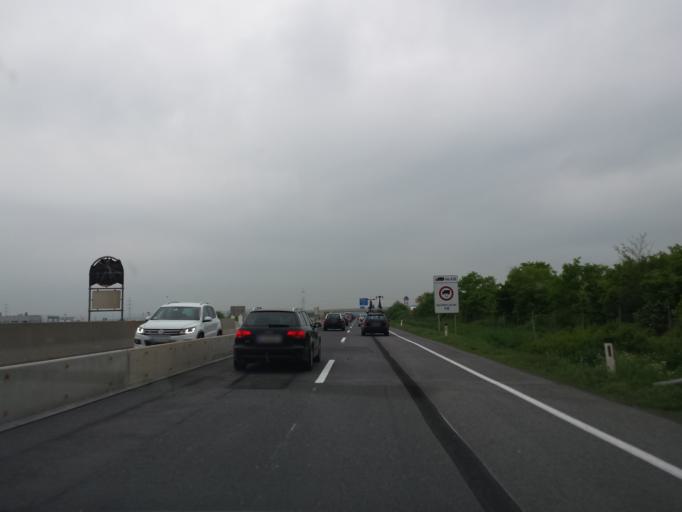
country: AT
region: Burgenland
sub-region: Politischer Bezirk Neusiedl am See
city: Parndorf
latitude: 47.9724
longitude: 16.8616
